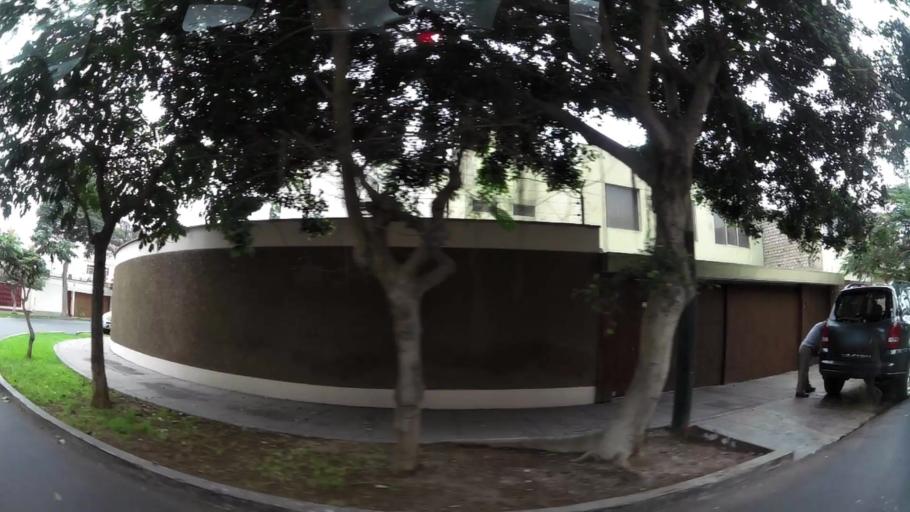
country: PE
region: Lima
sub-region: Lima
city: Surco
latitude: -12.1271
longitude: -76.9927
